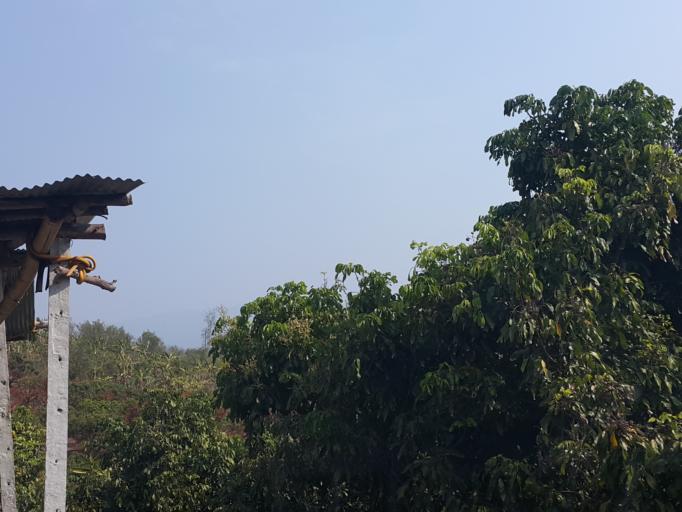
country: TH
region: Chiang Mai
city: Hang Dong
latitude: 18.7351
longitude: 98.8574
